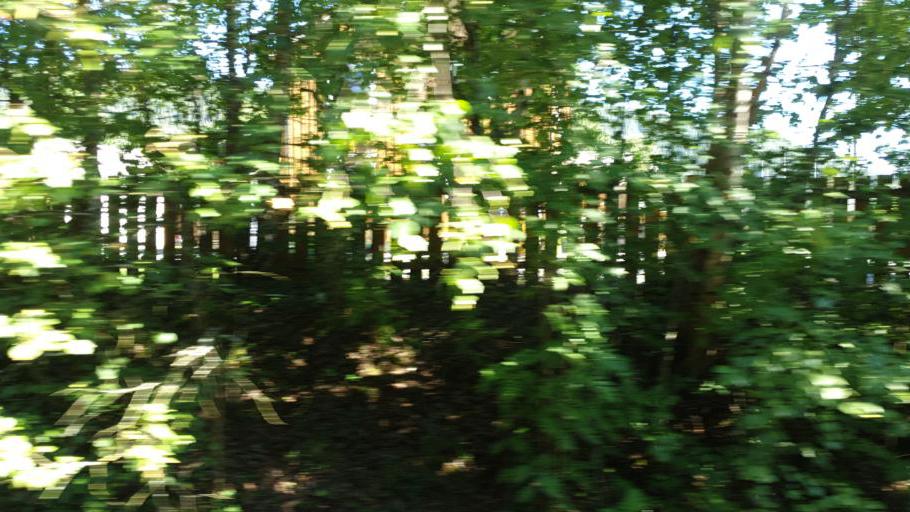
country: NO
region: Sor-Trondelag
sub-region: Orkdal
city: Orkanger
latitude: 63.2777
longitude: 9.8262
